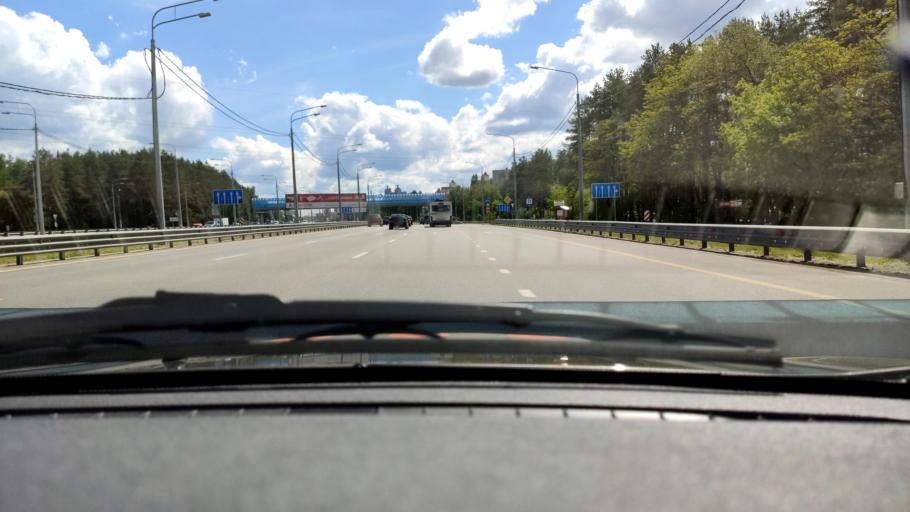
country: RU
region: Voronezj
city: Podgornoye
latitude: 51.7311
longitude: 39.1780
